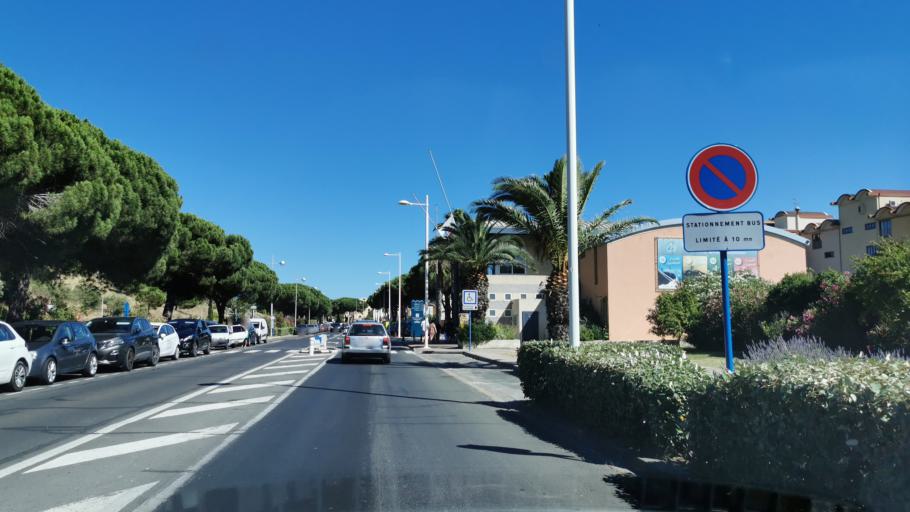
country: FR
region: Languedoc-Roussillon
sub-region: Departement de l'Aude
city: Gruissan
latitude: 43.1115
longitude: 3.0951
